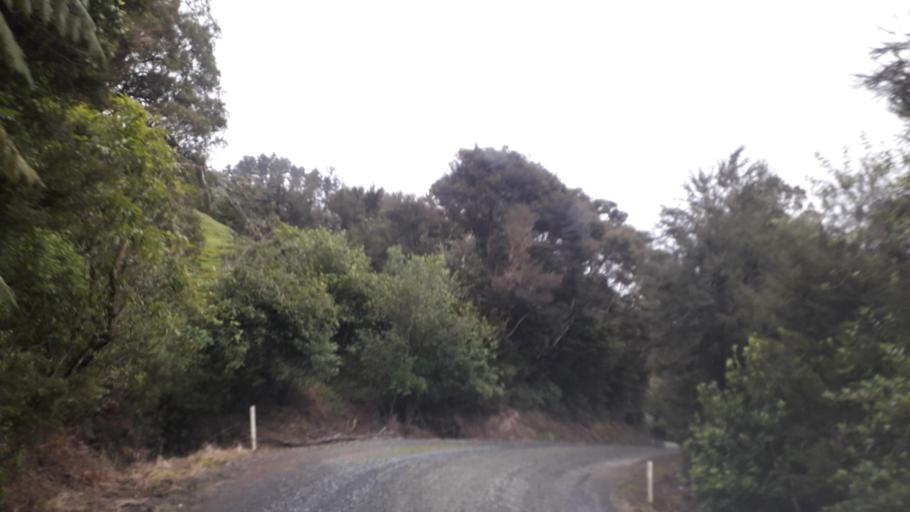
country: NZ
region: Northland
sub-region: Far North District
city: Waimate North
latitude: -35.1431
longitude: 173.7140
